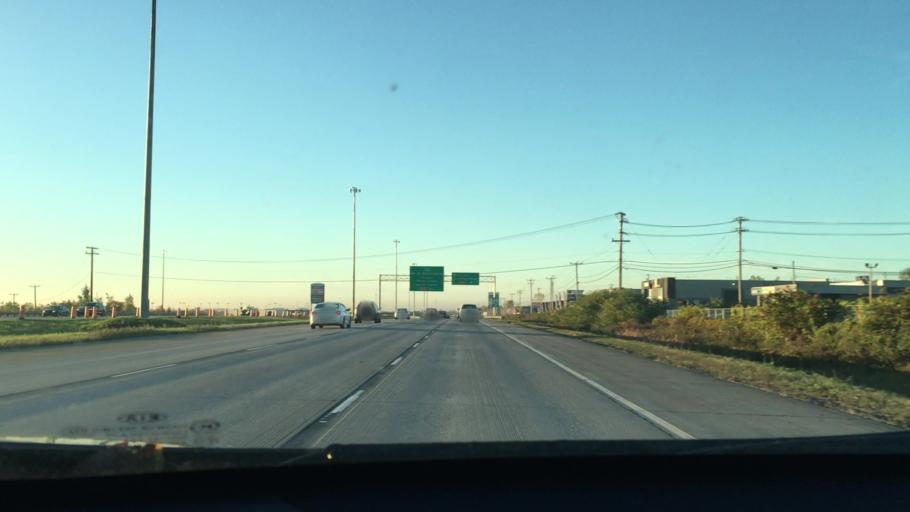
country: CA
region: Quebec
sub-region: Laurentides
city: Saint-Jerome
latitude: 45.7664
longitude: -74.0209
